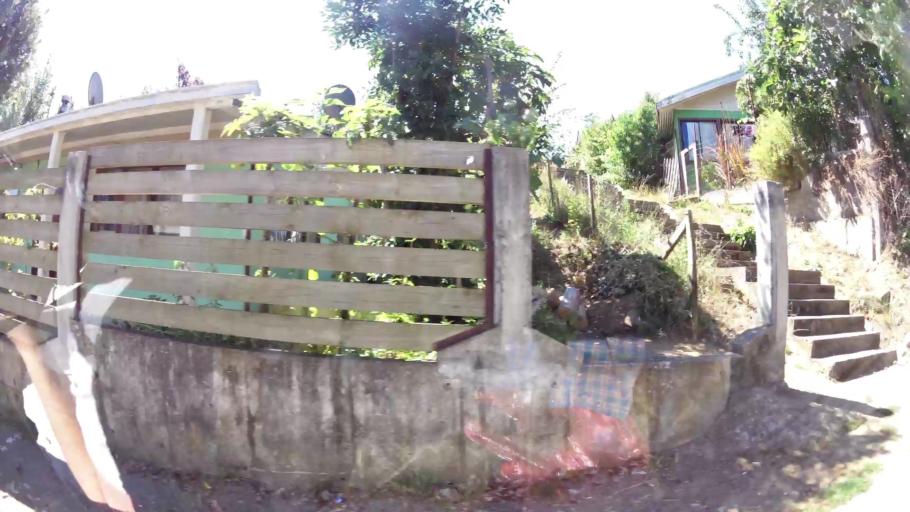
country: CL
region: Biobio
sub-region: Provincia de Concepcion
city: Penco
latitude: -36.7387
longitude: -72.9869
